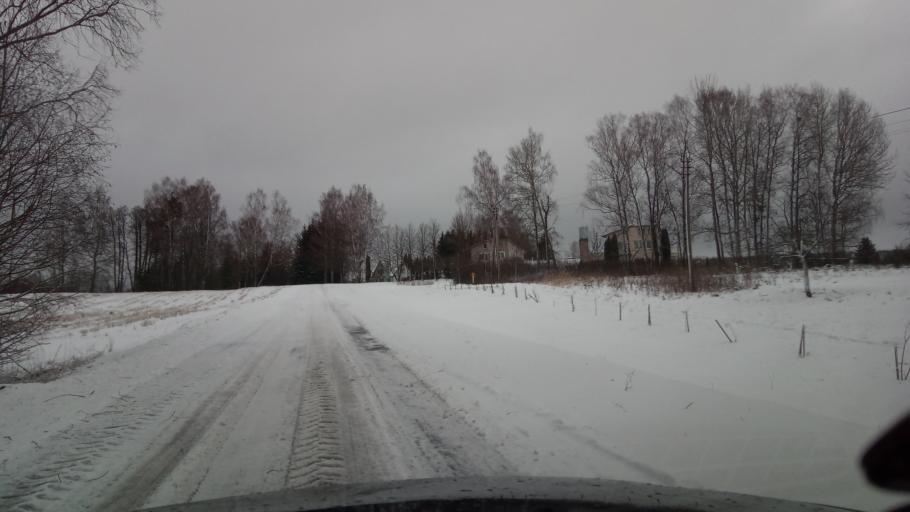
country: LT
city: Zarasai
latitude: 55.6238
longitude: 25.9555
